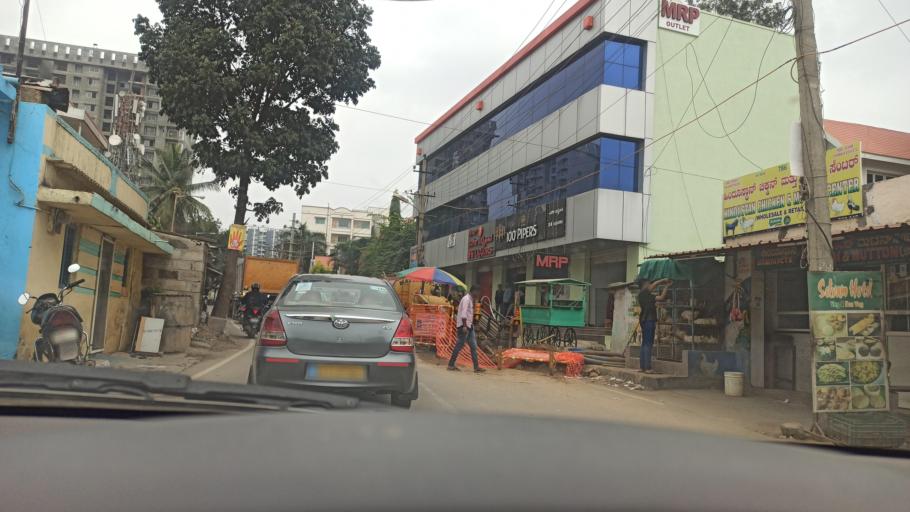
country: IN
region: Karnataka
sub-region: Bangalore Urban
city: Bangalore
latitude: 12.9927
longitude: 77.6889
